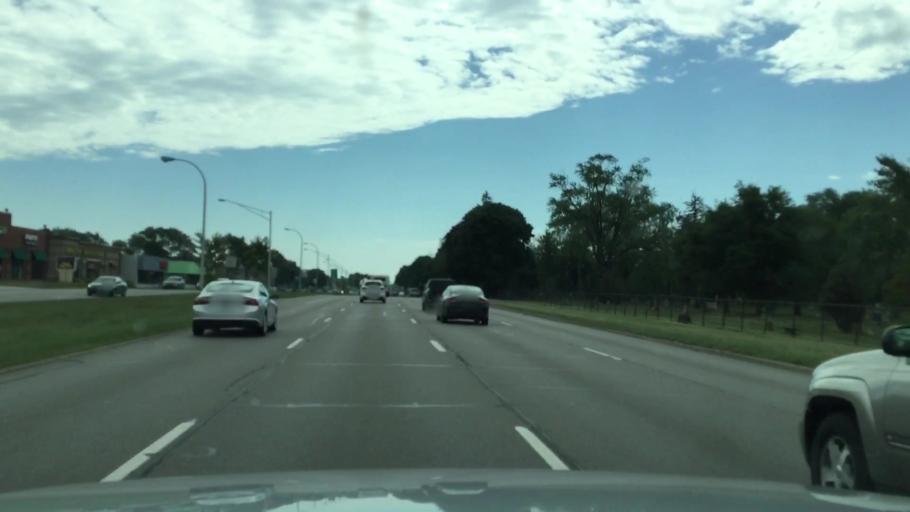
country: US
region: Michigan
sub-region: Oakland County
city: Berkley
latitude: 42.5079
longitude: -83.1768
